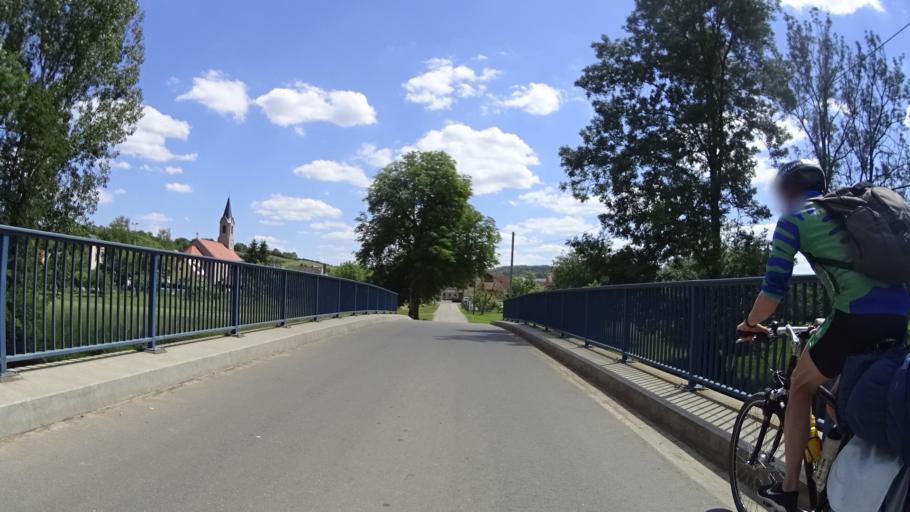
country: DE
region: Bavaria
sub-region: Regierungsbezirk Unterfranken
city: Bieberehren
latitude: 49.5158
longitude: 10.0047
